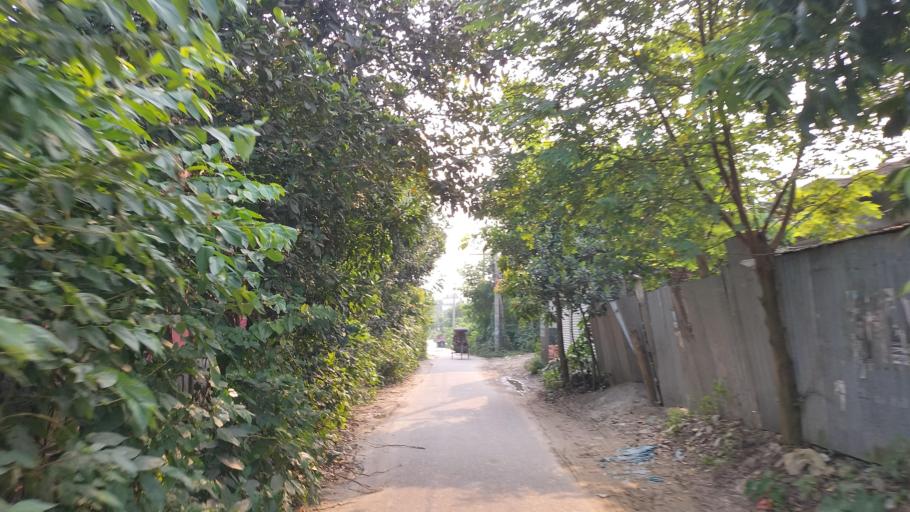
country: BD
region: Dhaka
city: Azimpur
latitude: 23.6736
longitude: 90.3127
